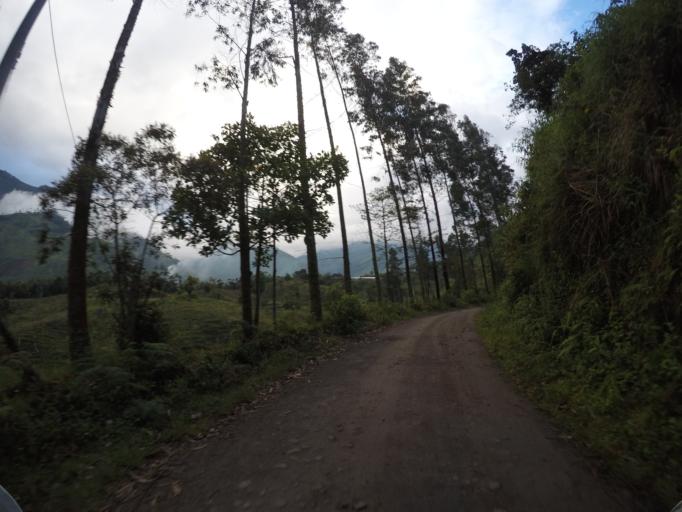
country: CO
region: Tolima
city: Cajamarca
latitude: 4.5154
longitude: -75.4043
